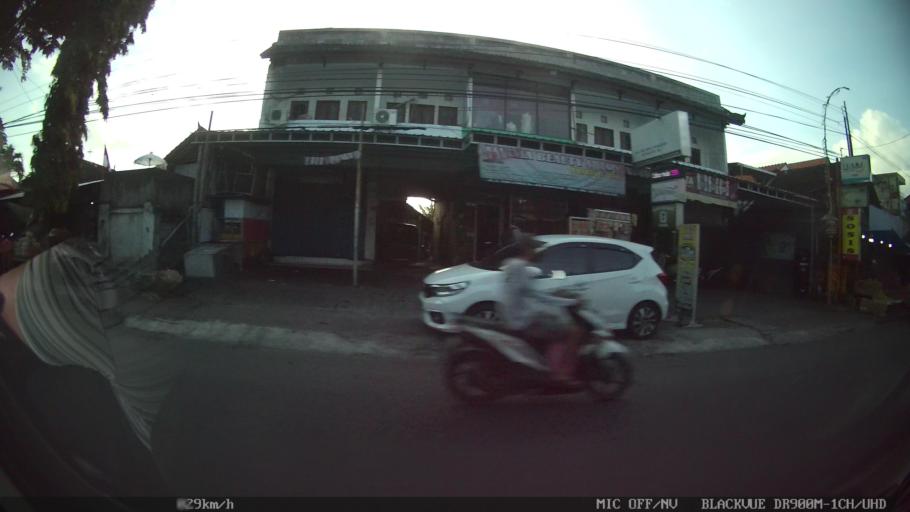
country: ID
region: Bali
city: Banjar Kertasari
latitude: -8.6256
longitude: 115.2083
